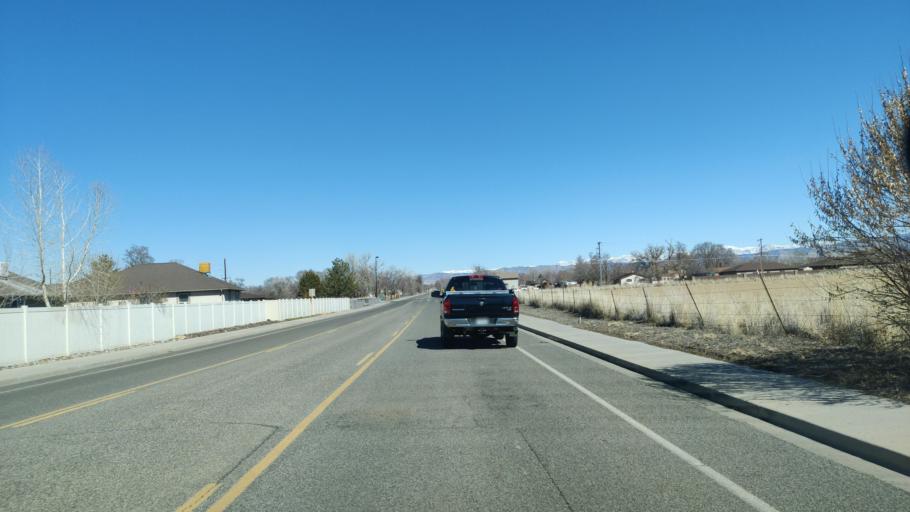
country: US
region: Colorado
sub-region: Mesa County
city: Fruita
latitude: 39.1627
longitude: -108.7197
